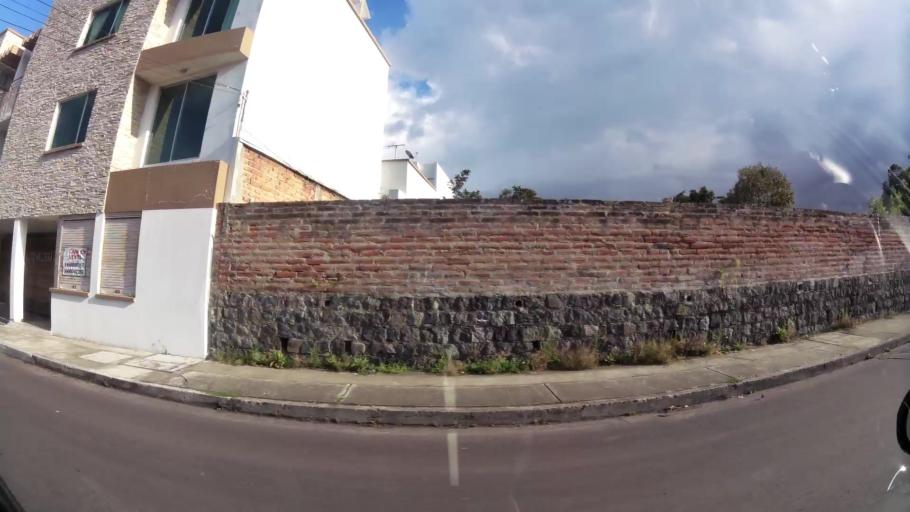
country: EC
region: Pichincha
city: Sangolqui
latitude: -0.2986
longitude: -78.4678
